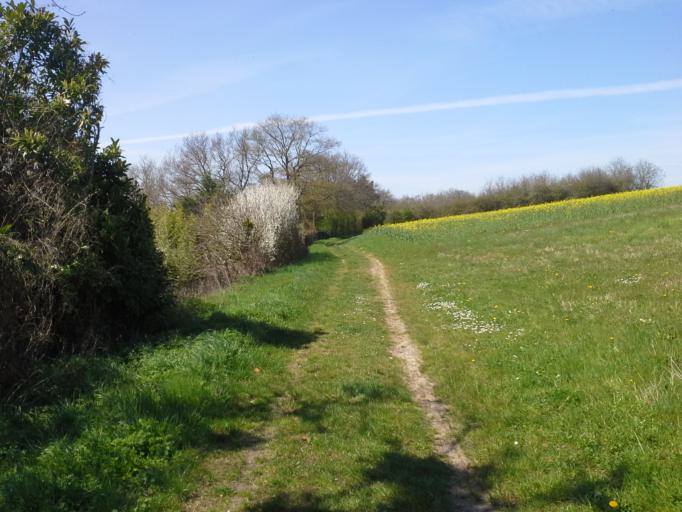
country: FR
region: Centre
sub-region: Departement du Loir-et-Cher
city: Villiers-sur-Loir
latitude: 47.8101
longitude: 0.9869
